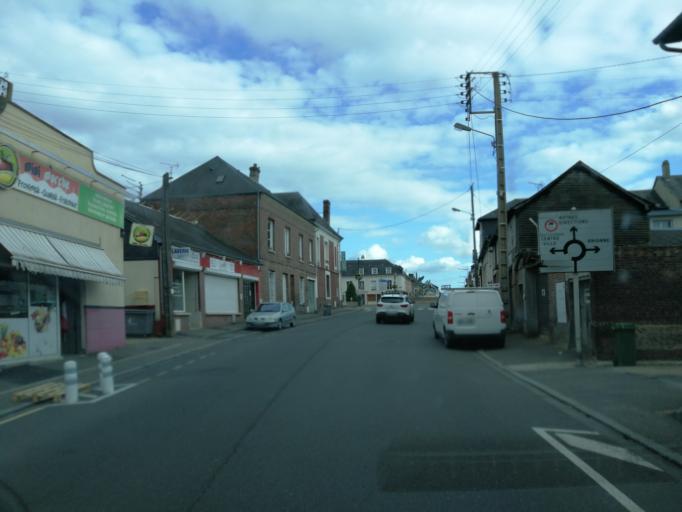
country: FR
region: Haute-Normandie
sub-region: Departement de l'Eure
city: Le Neubourg
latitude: 49.1491
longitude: 0.9003
